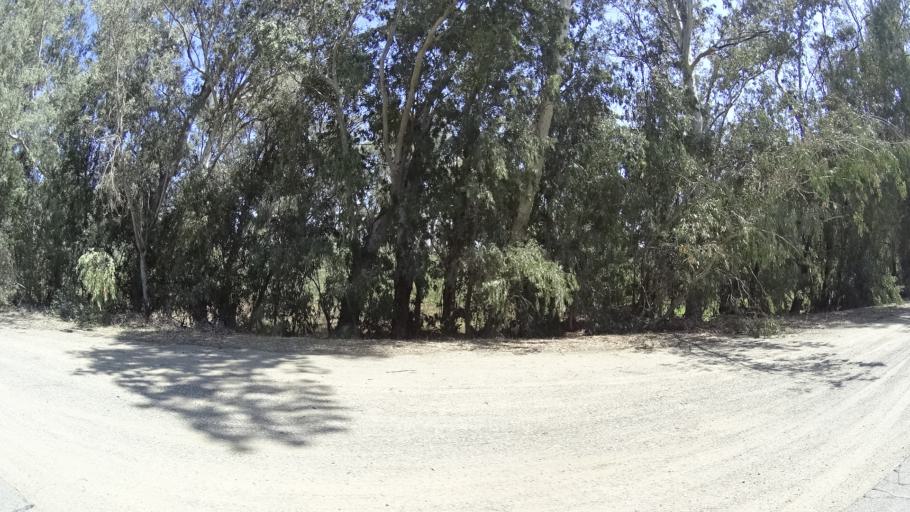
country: US
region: California
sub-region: Glenn County
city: Willows
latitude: 39.5866
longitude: -122.1946
